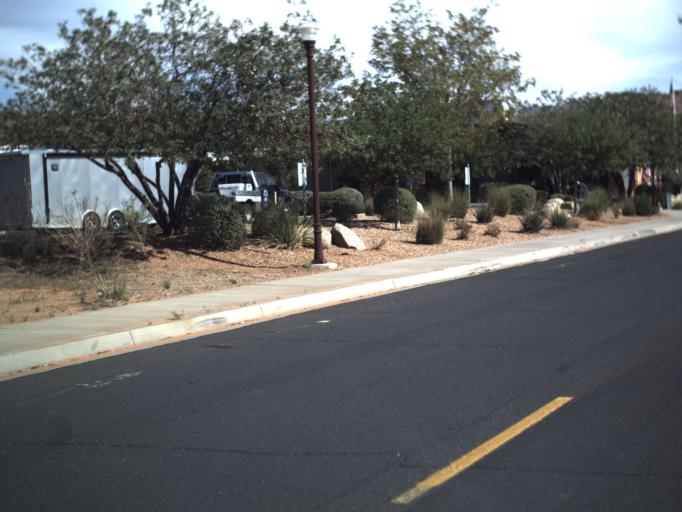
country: US
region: Utah
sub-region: Washington County
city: Washington
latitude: 37.1630
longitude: -113.4471
